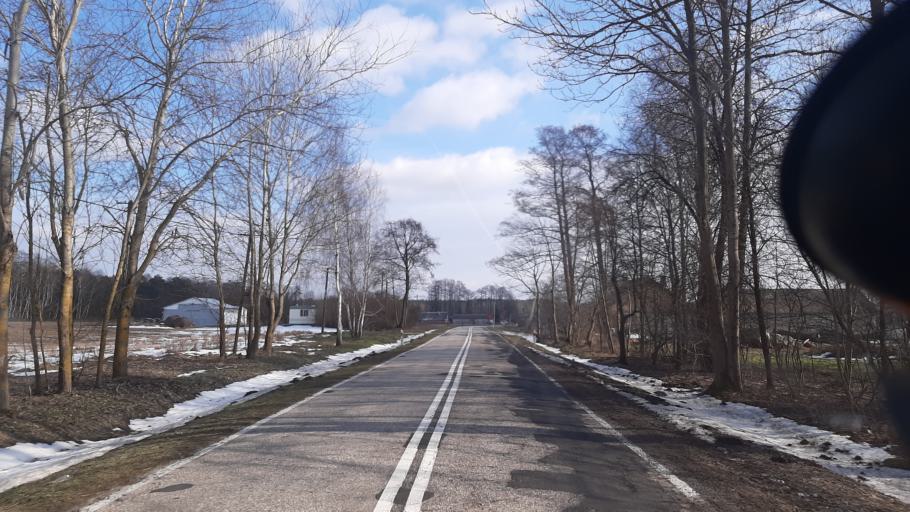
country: PL
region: Lublin Voivodeship
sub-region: Powiat wlodawski
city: Urszulin
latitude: 51.4987
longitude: 23.2552
